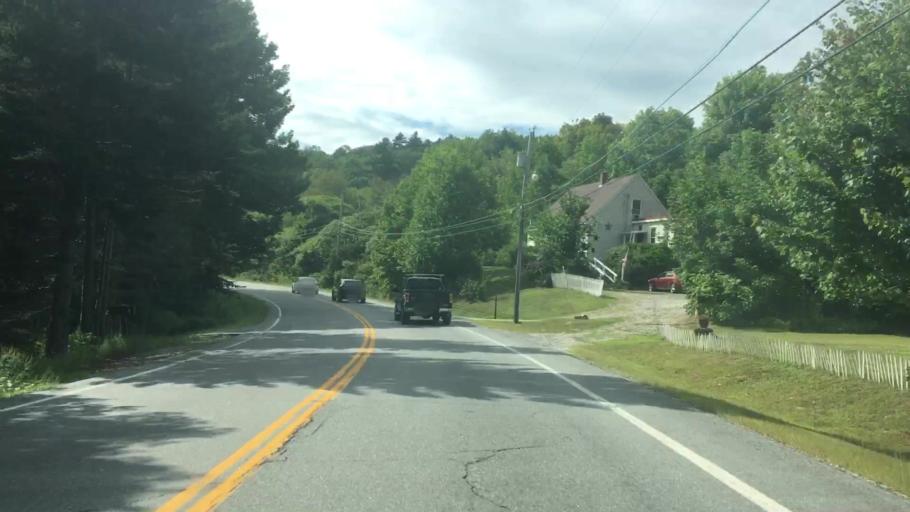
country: US
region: Maine
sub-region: Cumberland County
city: Raymond
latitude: 43.9865
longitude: -70.4862
